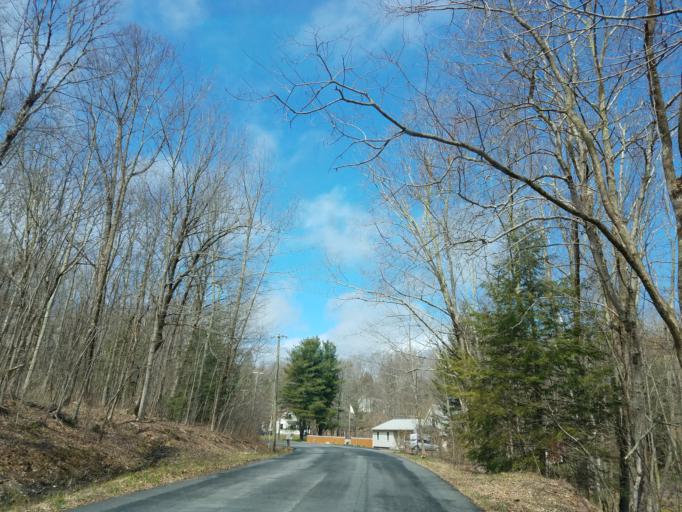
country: US
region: Connecticut
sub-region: Litchfield County
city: West Torrington
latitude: 41.7820
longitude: -73.1612
